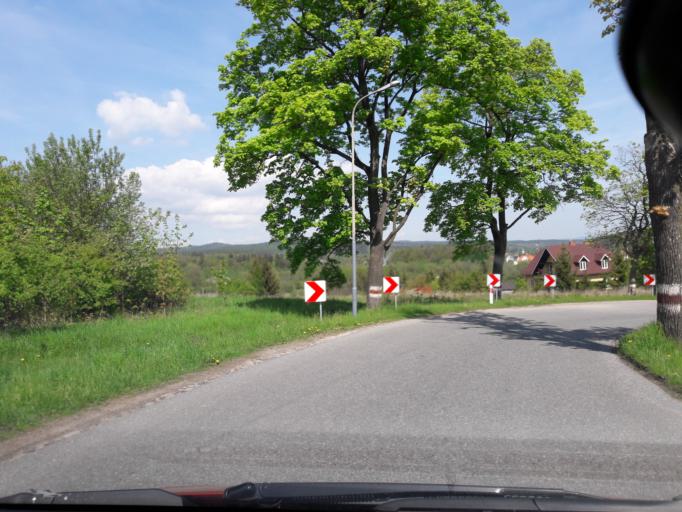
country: PL
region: Lower Silesian Voivodeship
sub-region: Powiat klodzki
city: Polanica-Zdroj
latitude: 50.3874
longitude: 16.5220
